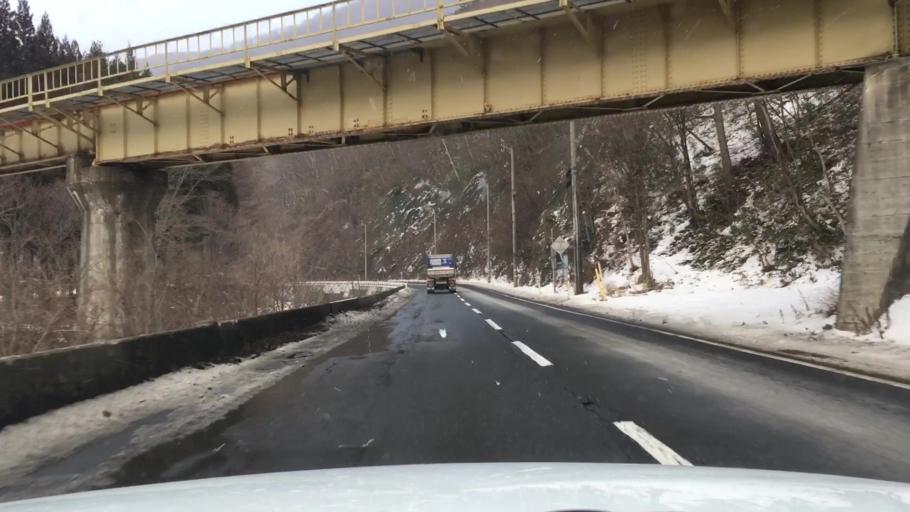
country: JP
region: Iwate
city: Tono
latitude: 39.6164
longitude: 141.4756
